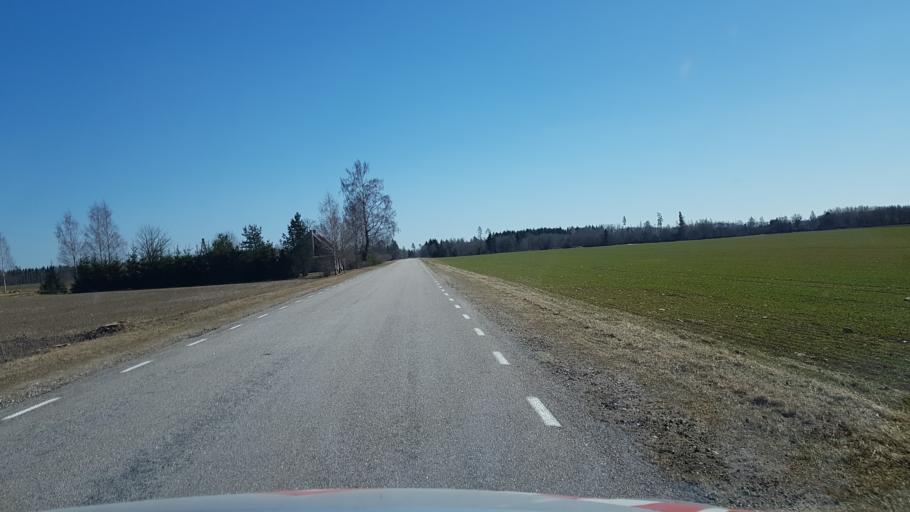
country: EE
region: Laeaene-Virumaa
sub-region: Vaeike-Maarja vald
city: Vaike-Maarja
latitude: 59.1019
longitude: 26.3922
